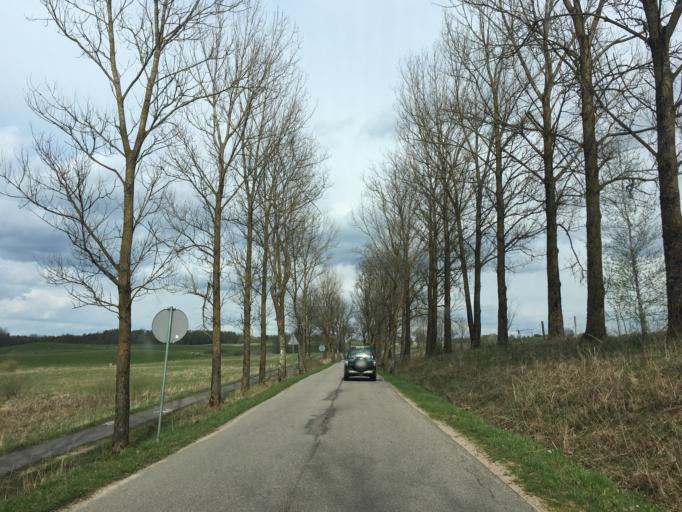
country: PL
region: Podlasie
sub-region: Powiat suwalski
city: Filipow
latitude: 54.3571
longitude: 22.7712
